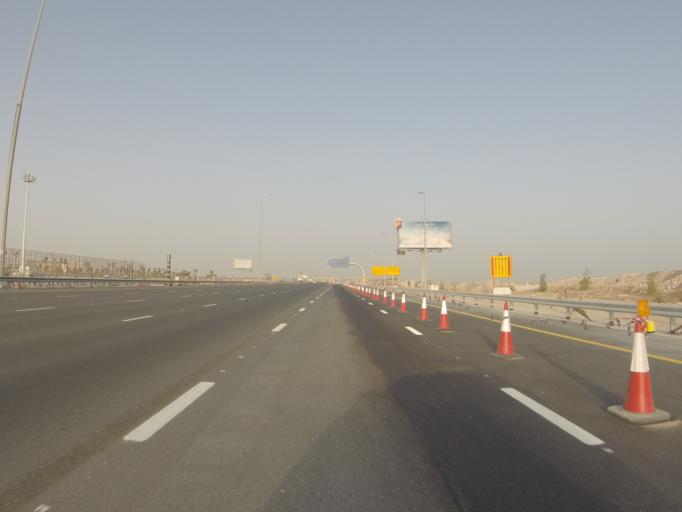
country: AE
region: Dubai
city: Dubai
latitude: 24.9239
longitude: 54.9942
